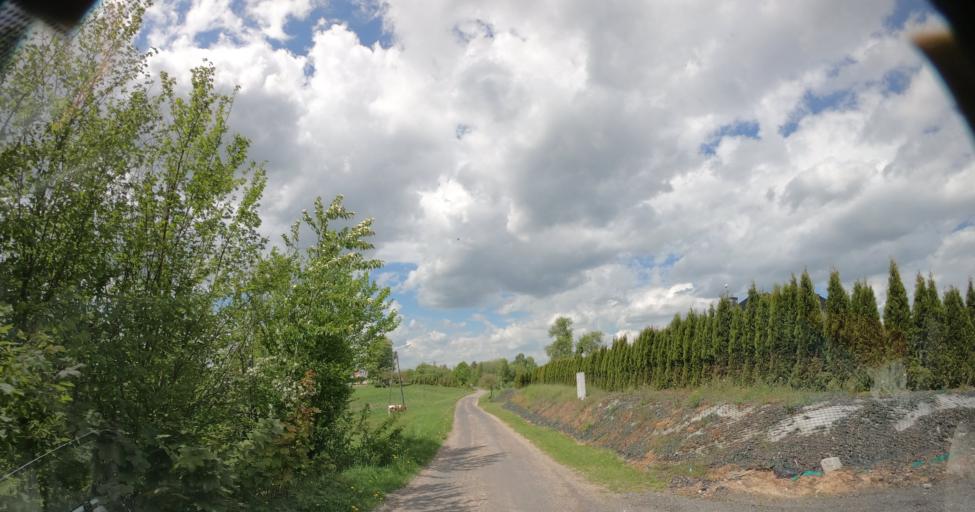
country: PL
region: West Pomeranian Voivodeship
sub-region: Powiat drawski
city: Drawsko Pomorskie
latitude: 53.5744
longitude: 15.7659
